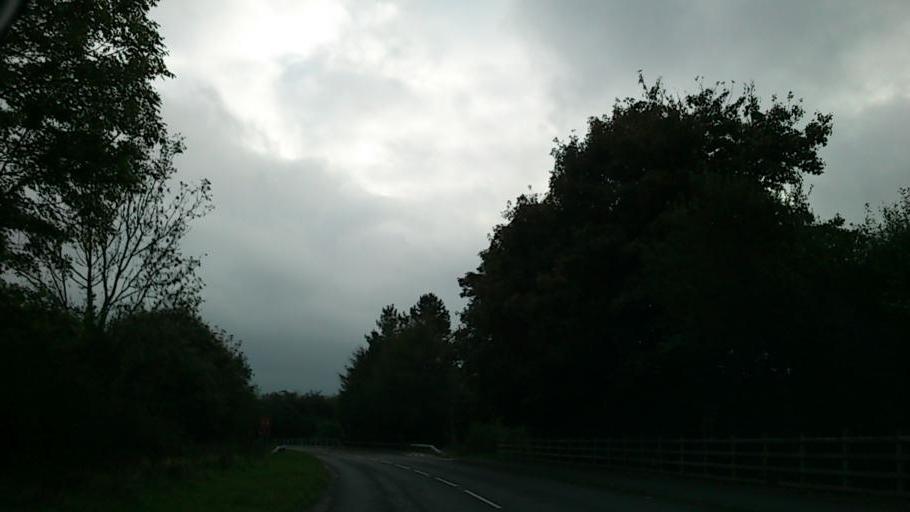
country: GB
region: Wales
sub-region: Sir Powys
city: Machynlleth
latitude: 52.5912
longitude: -3.8340
